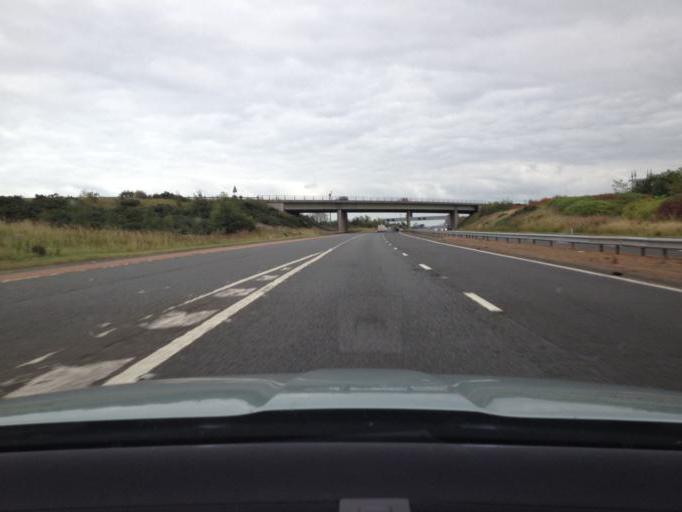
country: GB
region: Scotland
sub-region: Fife
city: Crossgates
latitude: 56.0794
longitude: -3.3947
